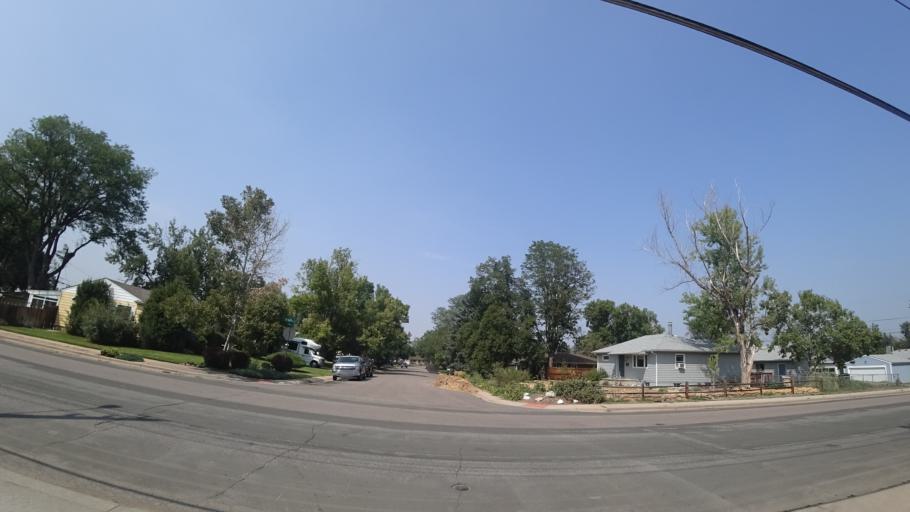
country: US
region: Colorado
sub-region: Arapahoe County
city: Englewood
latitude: 39.6330
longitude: -104.9995
